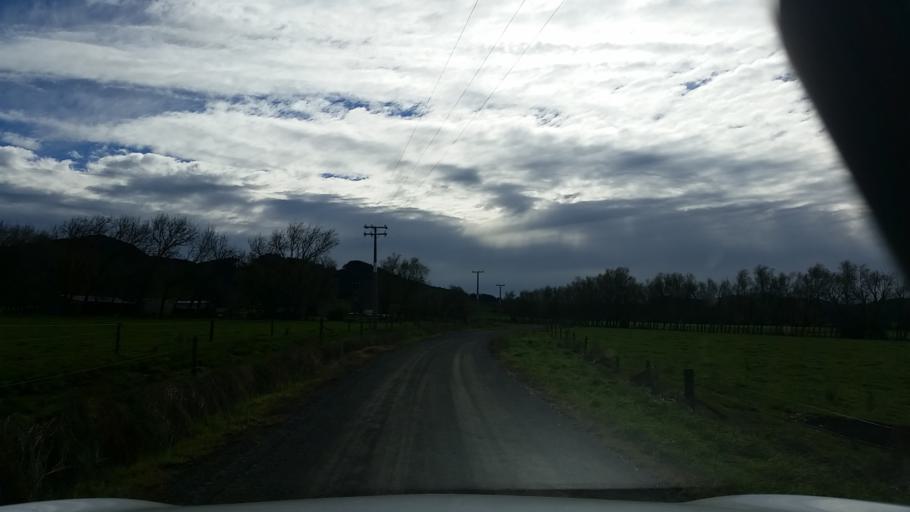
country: NZ
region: Waikato
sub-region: Hauraki District
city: Ngatea
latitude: -37.5061
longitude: 175.4068
